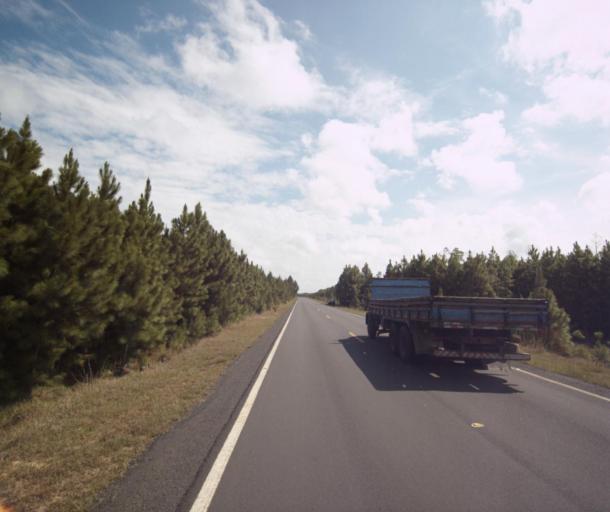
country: BR
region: Rio Grande do Sul
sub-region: Sao Lourenco Do Sul
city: Sao Lourenco do Sul
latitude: -31.4567
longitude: -51.2212
